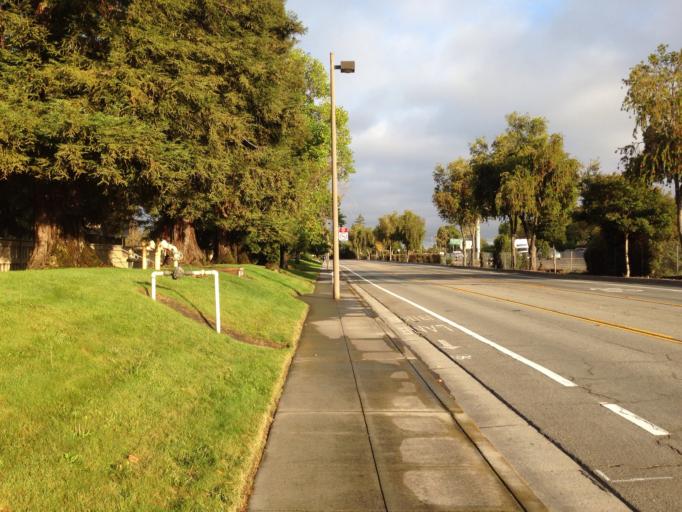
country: US
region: California
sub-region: Santa Clara County
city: Santa Clara
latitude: 37.3887
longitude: -121.9888
